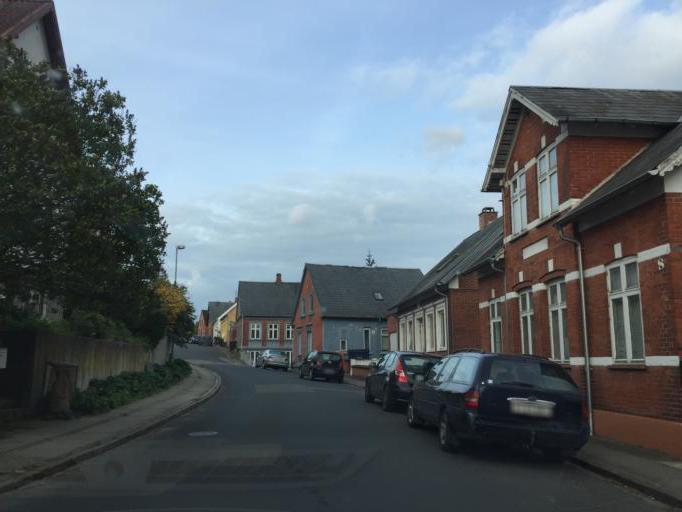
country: DK
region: South Denmark
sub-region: Svendborg Kommune
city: Svendborg
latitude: 55.0638
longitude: 10.6056
